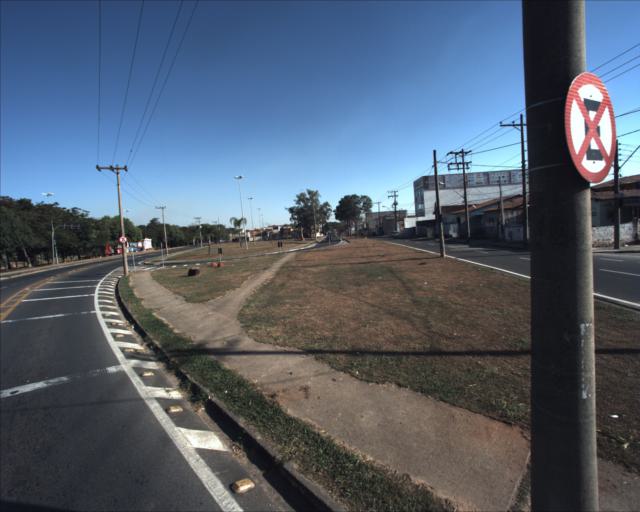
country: BR
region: Sao Paulo
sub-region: Sorocaba
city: Sorocaba
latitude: -23.4686
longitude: -47.4414
